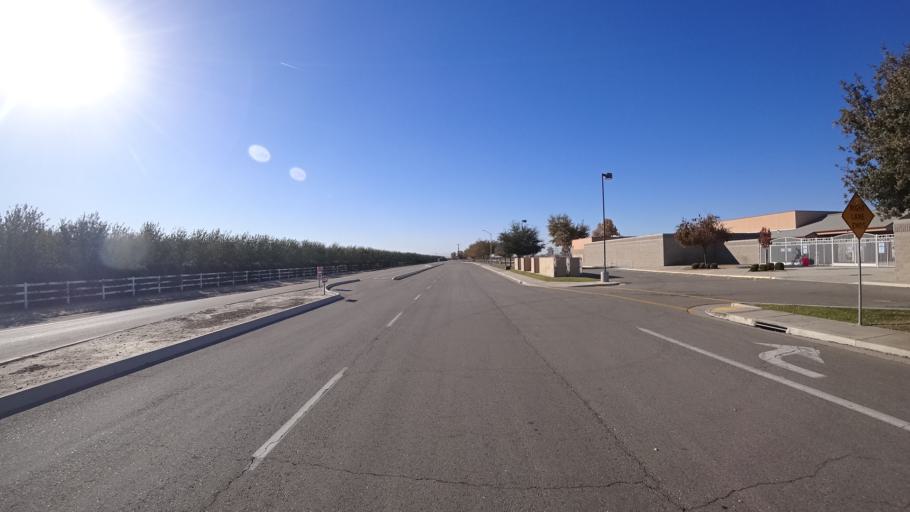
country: US
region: California
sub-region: Kern County
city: Greenacres
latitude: 35.2818
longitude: -119.1121
